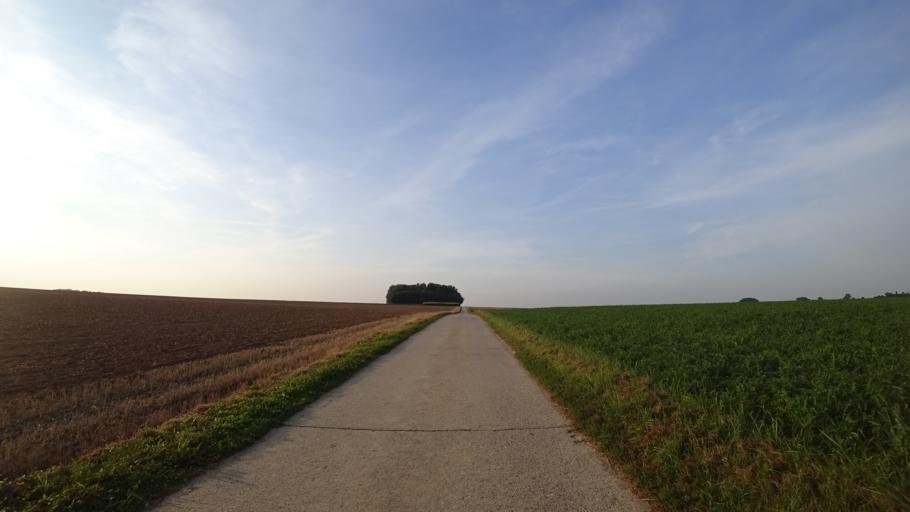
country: BE
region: Wallonia
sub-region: Province du Brabant Wallon
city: Walhain-Saint-Paul
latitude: 50.6164
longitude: 4.6811
